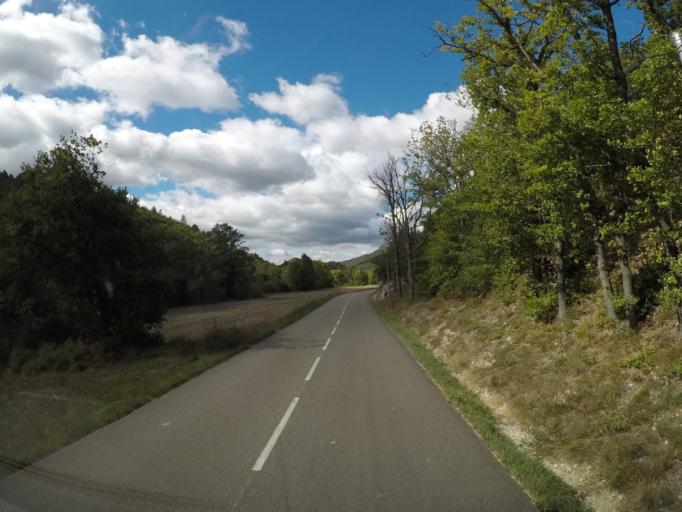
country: FR
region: Provence-Alpes-Cote d'Azur
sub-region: Departement du Vaucluse
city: Sault
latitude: 44.1794
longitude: 5.3958
